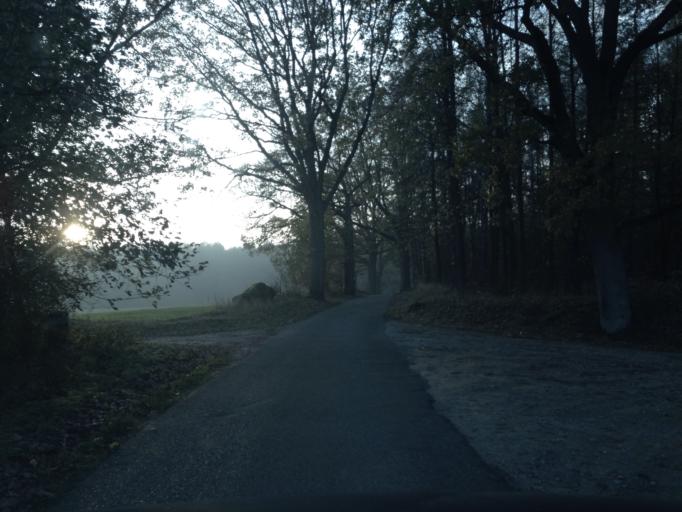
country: PL
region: Warmian-Masurian Voivodeship
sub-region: Powiat dzialdowski
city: Lidzbark
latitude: 53.2476
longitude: 19.7635
